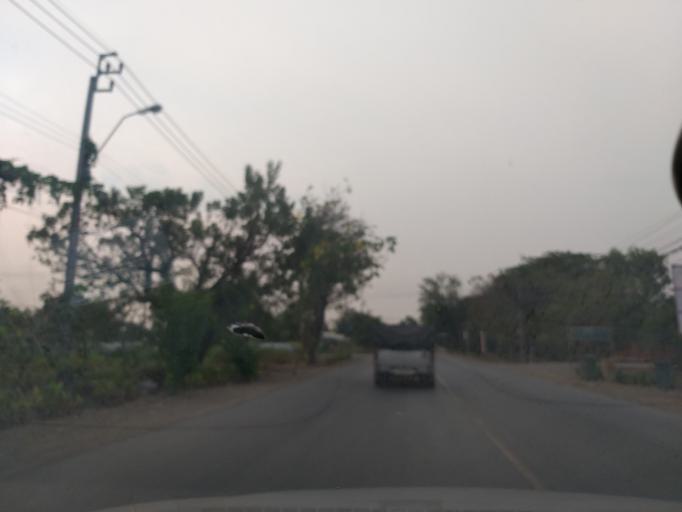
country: TH
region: Bangkok
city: Nong Chok
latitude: 13.8342
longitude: 100.9092
